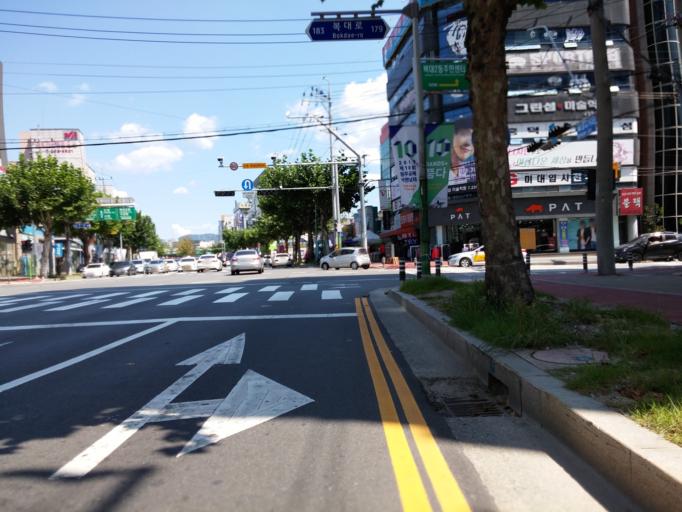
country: KR
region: Chungcheongbuk-do
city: Cheongju-si
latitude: 36.6327
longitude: 127.4404
